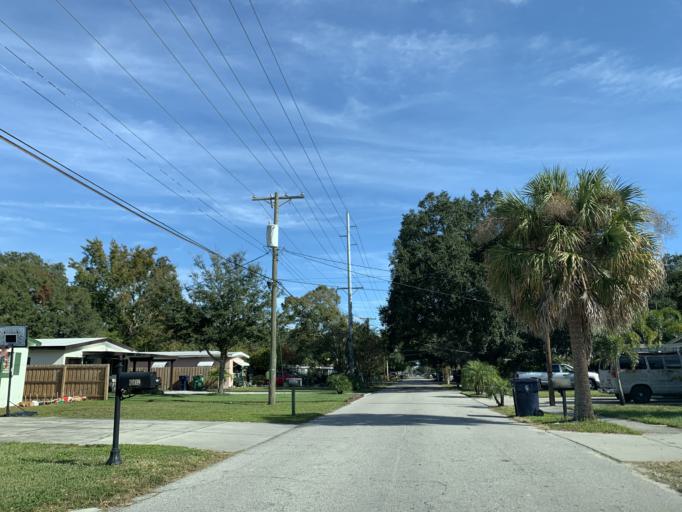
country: US
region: Florida
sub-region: Hillsborough County
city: Tampa
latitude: 27.8899
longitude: -82.4968
